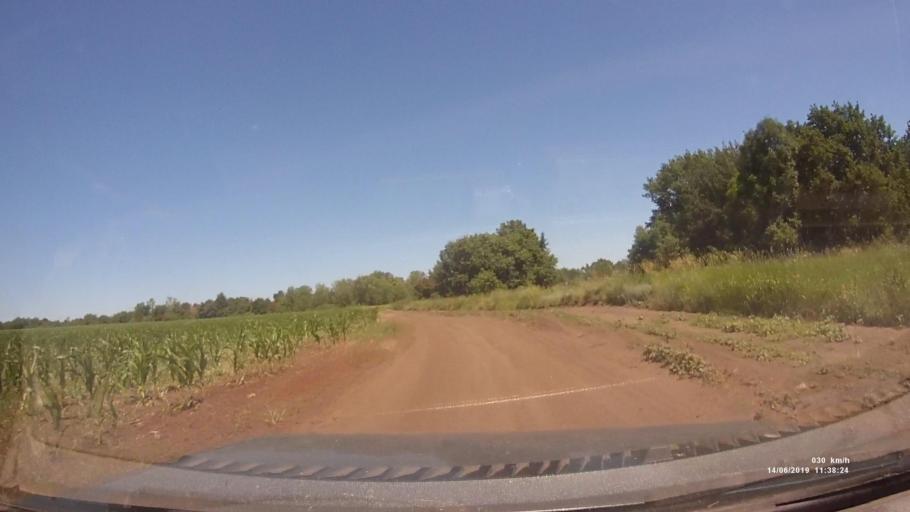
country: RU
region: Rostov
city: Kazanskaya
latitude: 49.8666
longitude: 41.3706
